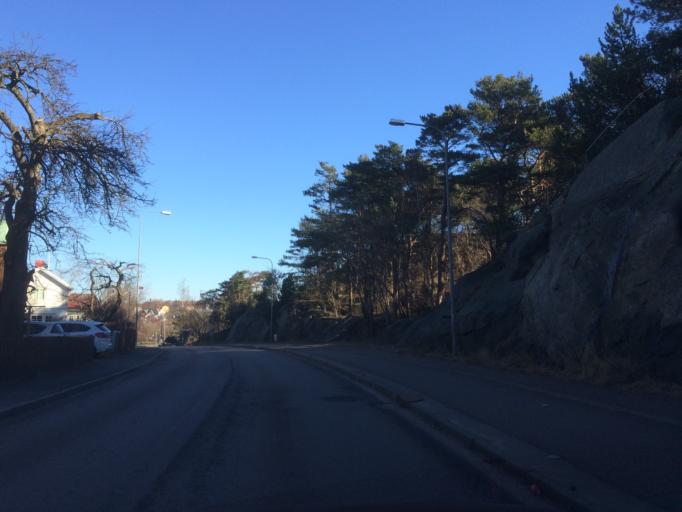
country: SE
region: Vaestra Goetaland
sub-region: Goteborg
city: Majorna
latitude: 57.6744
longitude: 11.8970
